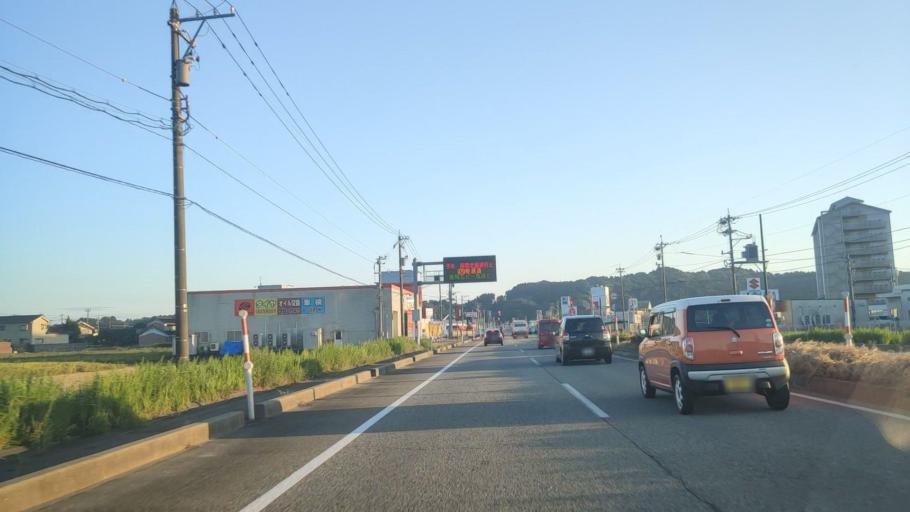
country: JP
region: Toyama
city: Himi
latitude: 36.8655
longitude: 136.9756
